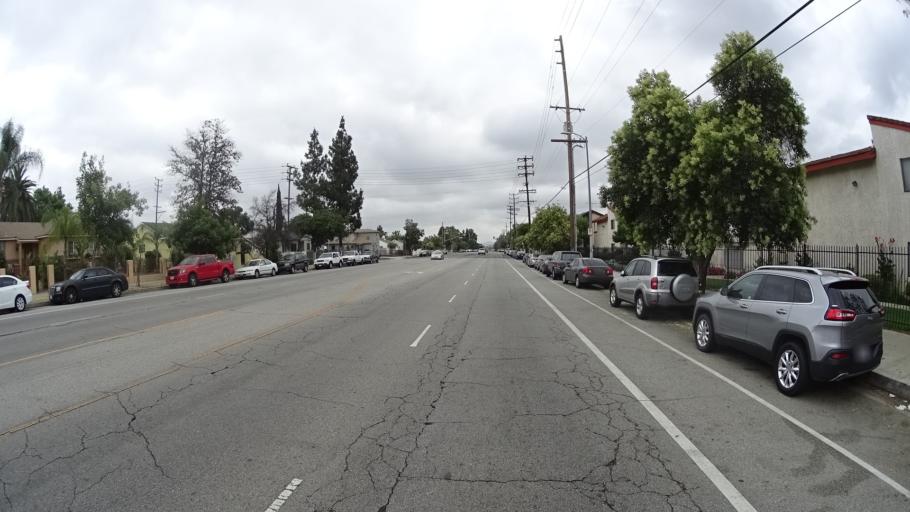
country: US
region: California
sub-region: Los Angeles County
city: San Fernando
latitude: 34.2442
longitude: -118.4464
